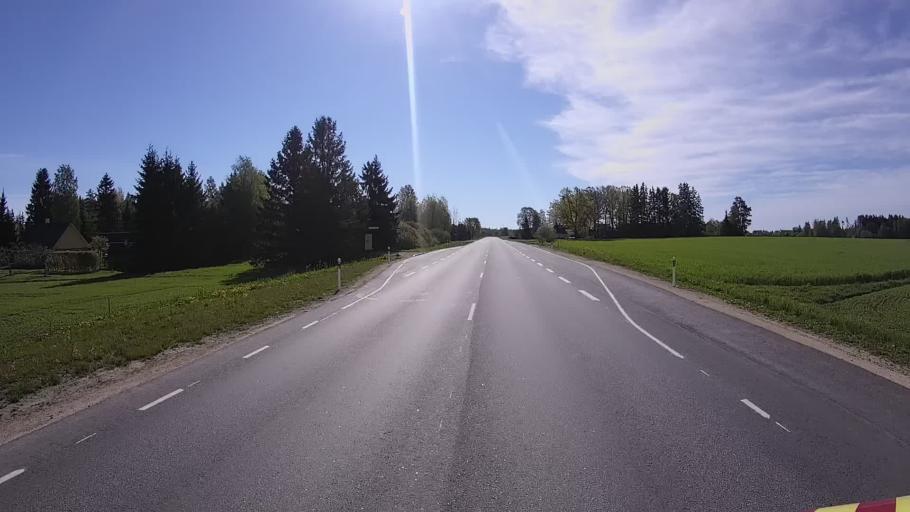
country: EE
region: Tartu
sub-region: UElenurme vald
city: Ulenurme
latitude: 58.3412
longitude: 26.9556
